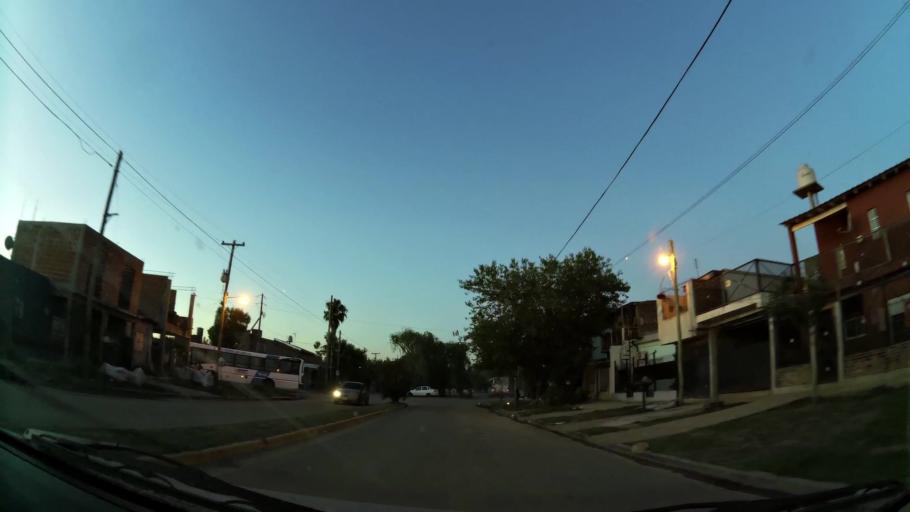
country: AR
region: Buenos Aires
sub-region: Partido de Almirante Brown
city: Adrogue
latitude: -34.7852
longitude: -58.3237
